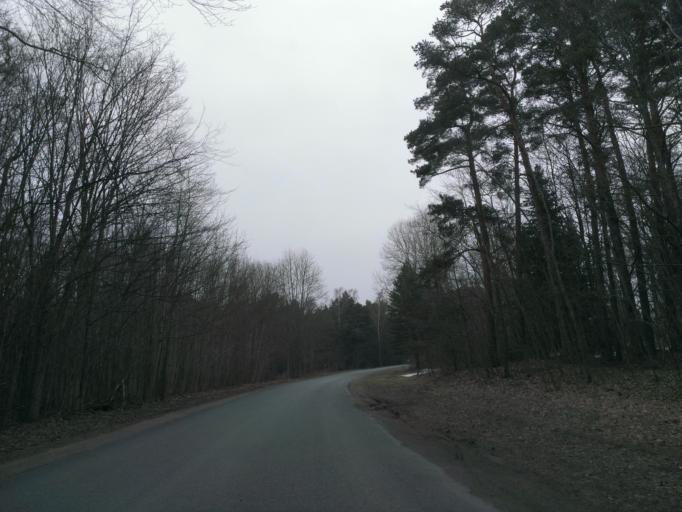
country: LV
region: Salacgrivas
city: Ainazi
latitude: 58.0168
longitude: 24.4511
